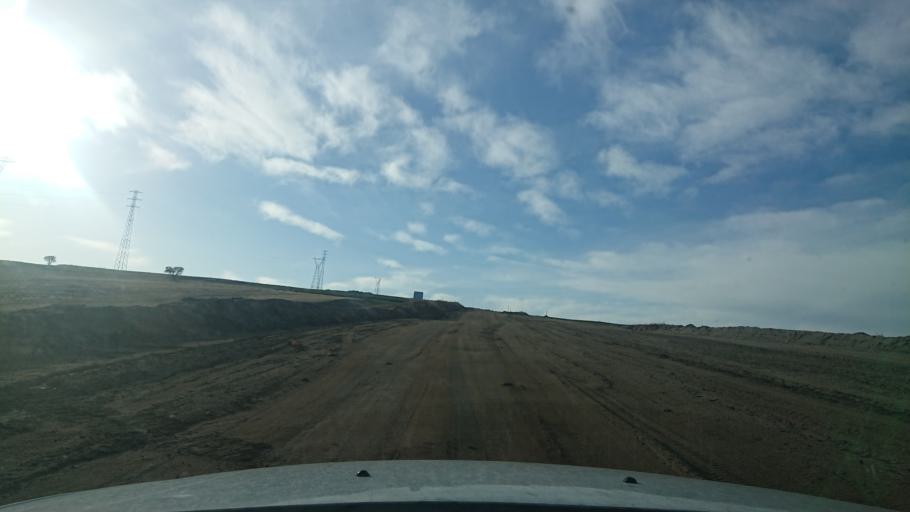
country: TR
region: Aksaray
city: Agacoren
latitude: 38.8529
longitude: 33.9429
